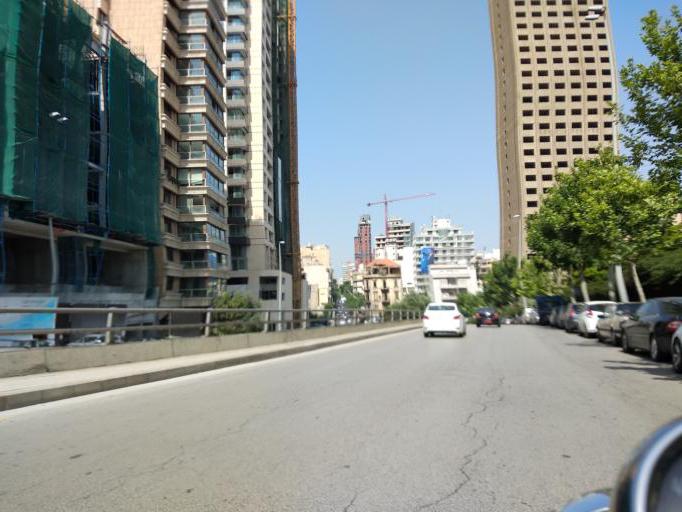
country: LB
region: Beyrouth
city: Beirut
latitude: 33.8949
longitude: 35.4980
